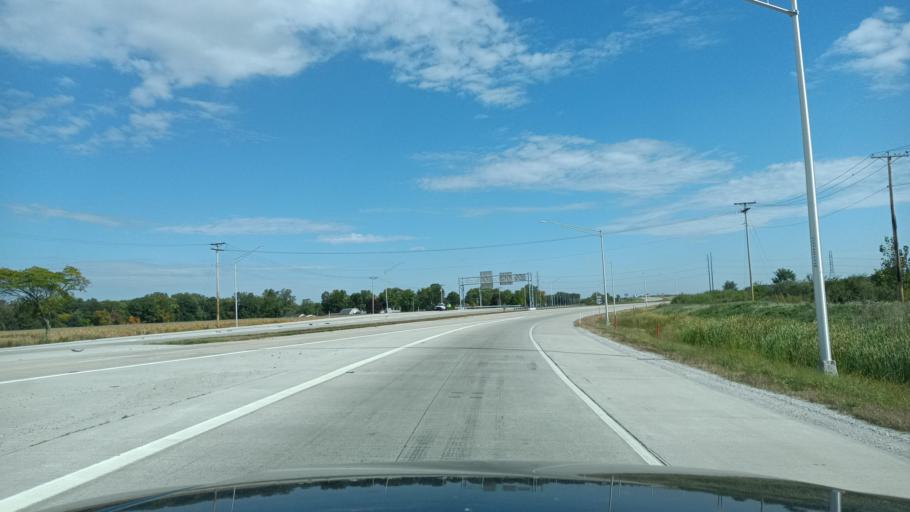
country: US
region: Indiana
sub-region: Allen County
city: New Haven
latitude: 41.0861
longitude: -84.9895
